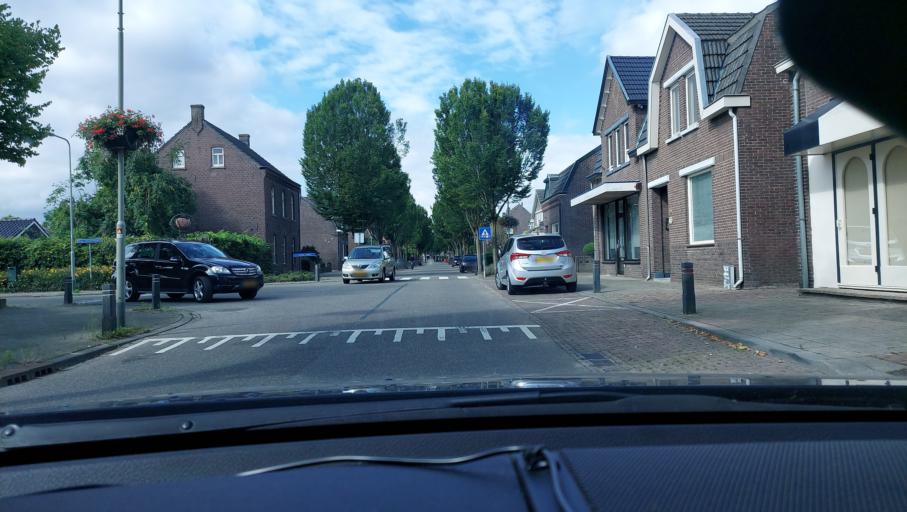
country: NL
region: Limburg
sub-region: Gemeente Beesel
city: Reuver
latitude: 51.2822
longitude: 6.0741
